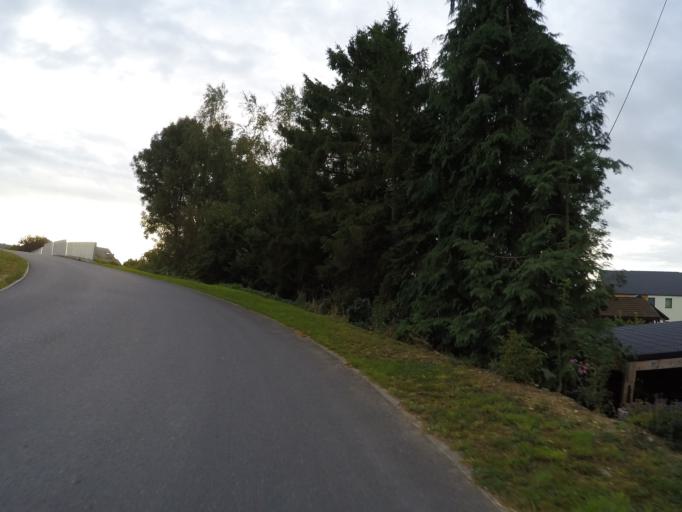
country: BE
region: Wallonia
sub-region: Province de Namur
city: Ciney
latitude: 50.3332
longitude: 5.0627
